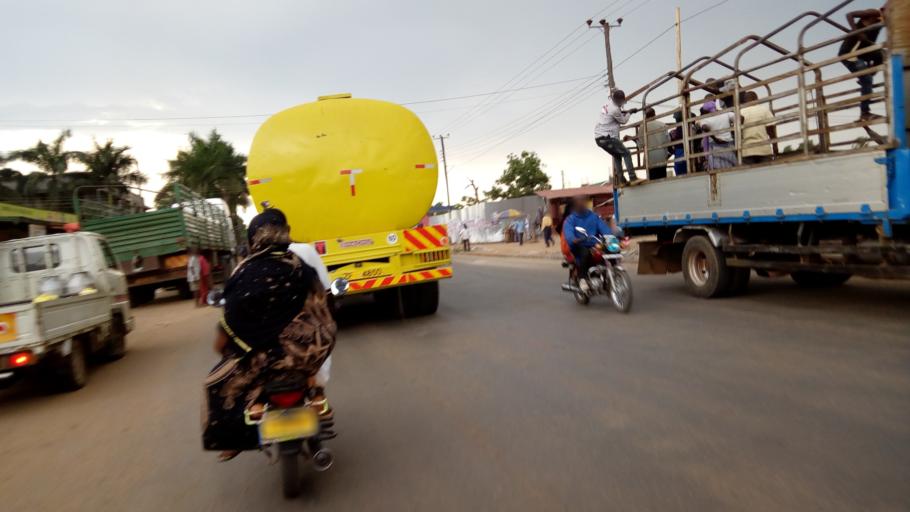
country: UG
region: Eastern Region
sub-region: Mbale District
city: Mbale
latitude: 1.0922
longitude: 34.1768
